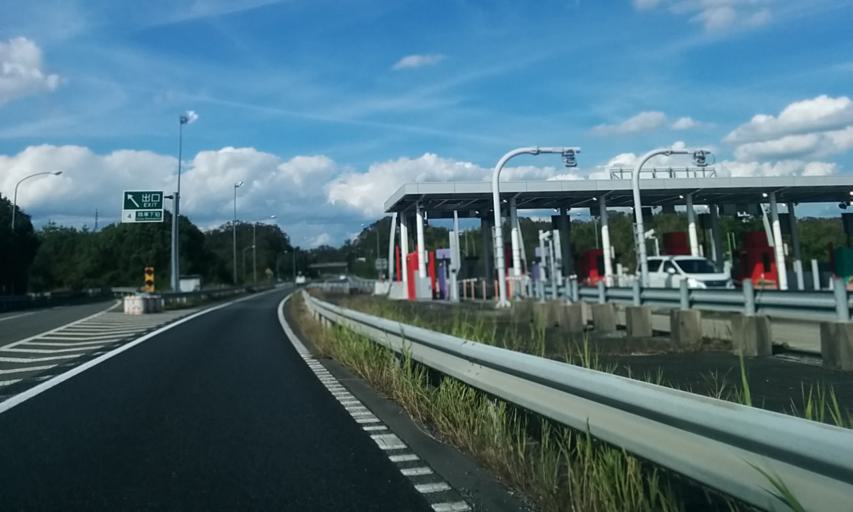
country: JP
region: Kyoto
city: Tanabe
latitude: 34.7752
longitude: 135.7734
